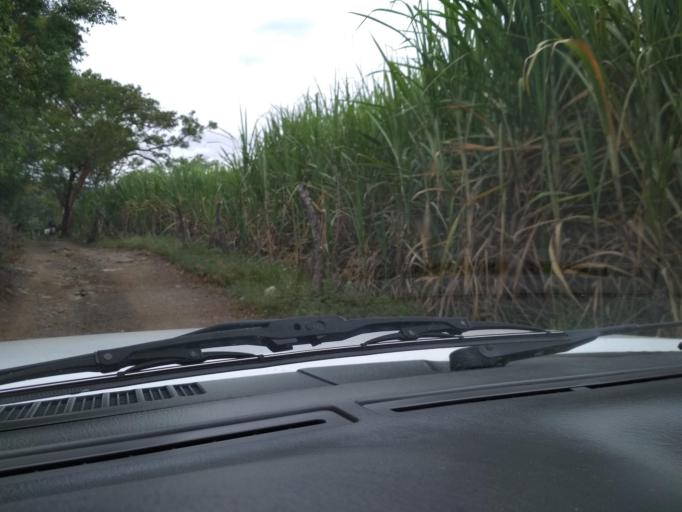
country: MX
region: Veracruz
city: Alto Lucero
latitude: 19.5926
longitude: -96.7832
